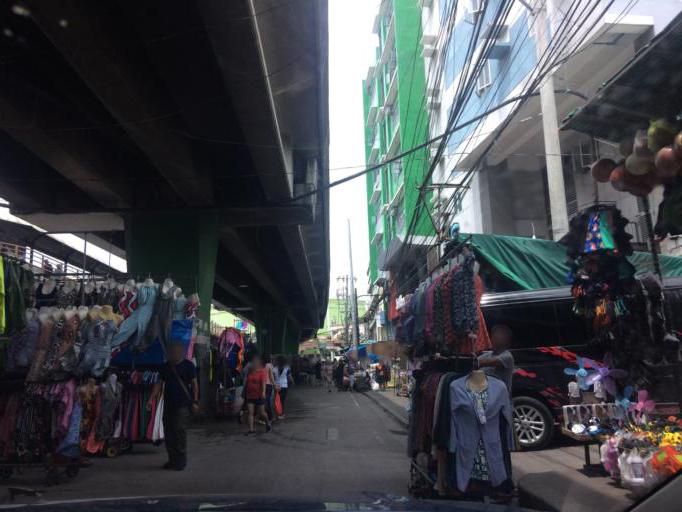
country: PH
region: Metro Manila
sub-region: Makati City
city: Makati City
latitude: 14.5362
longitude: 120.9999
